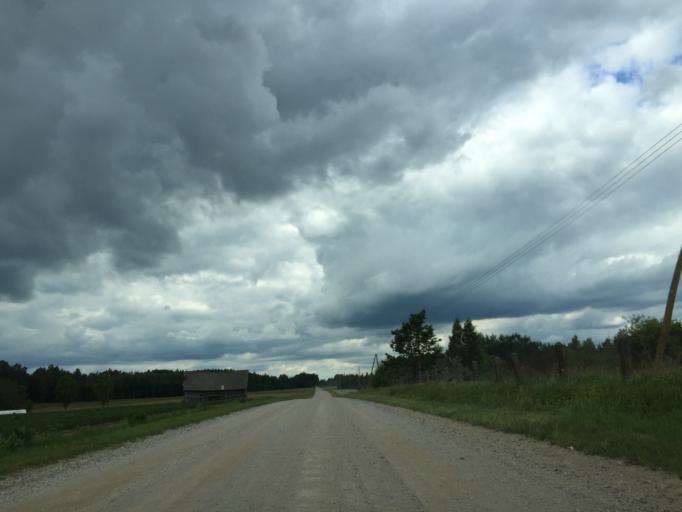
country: LV
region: Malpils
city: Malpils
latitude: 56.8638
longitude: 25.0146
